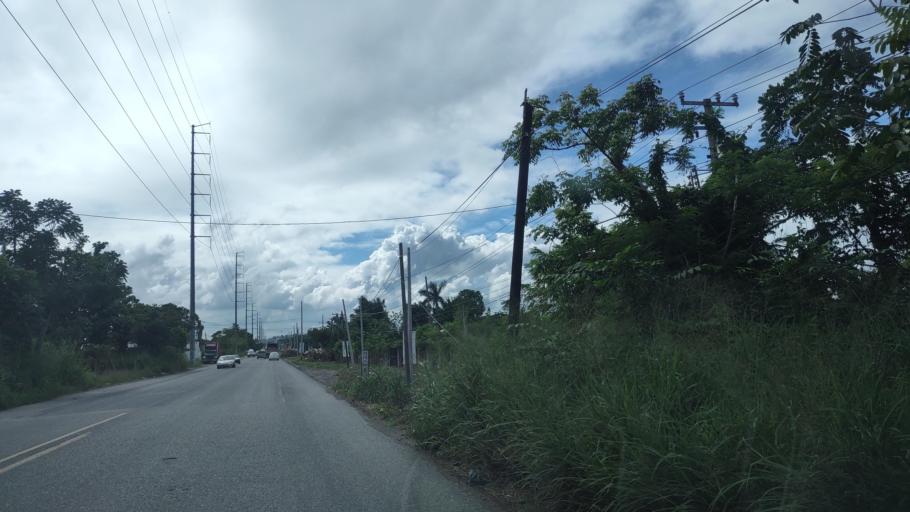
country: MX
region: Veracruz
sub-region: Papantla
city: Fraccionamiento la Florida
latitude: 20.5892
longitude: -97.4239
